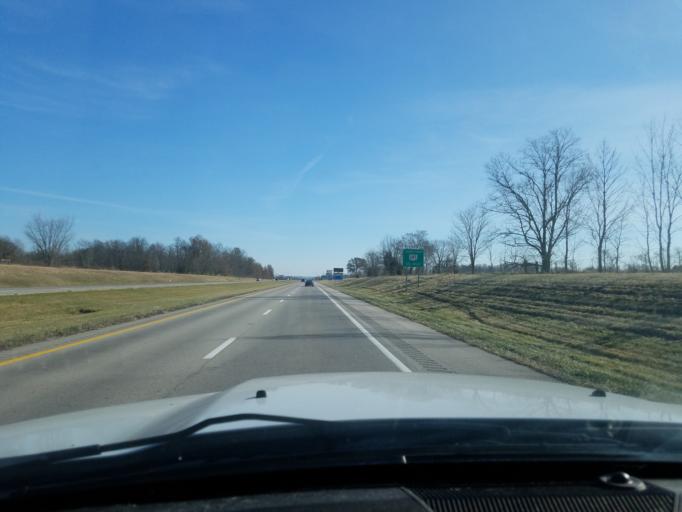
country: US
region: Ohio
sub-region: Adams County
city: Winchester
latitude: 38.9324
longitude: -83.5791
